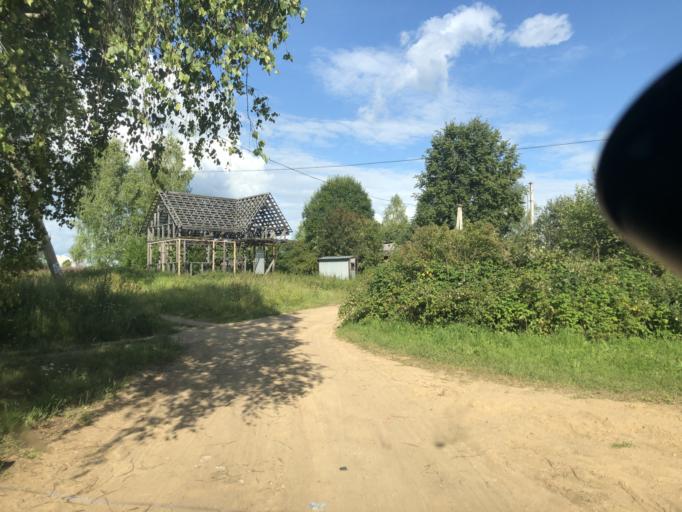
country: RU
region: Smolensk
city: Ugra
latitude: 54.8501
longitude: 34.5053
